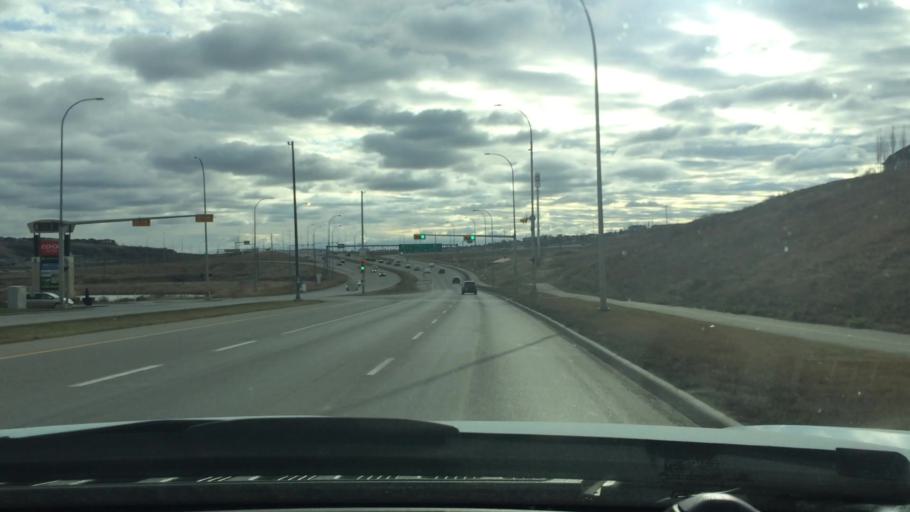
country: CA
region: Alberta
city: Calgary
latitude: 51.1603
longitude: -114.1244
